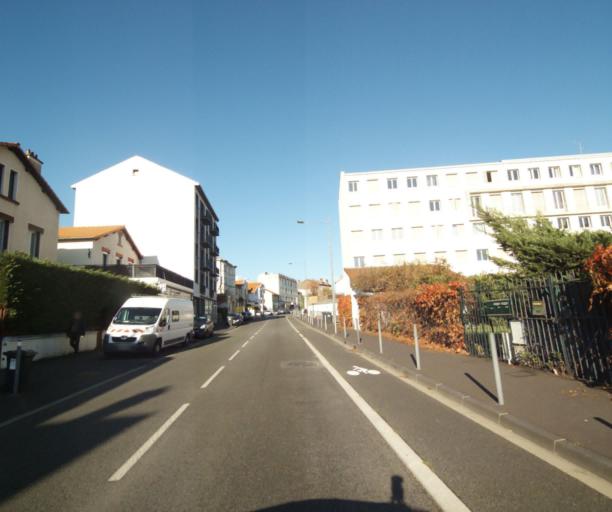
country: FR
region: Auvergne
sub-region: Departement du Puy-de-Dome
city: Clermont-Ferrand
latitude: 45.7650
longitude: 3.0974
